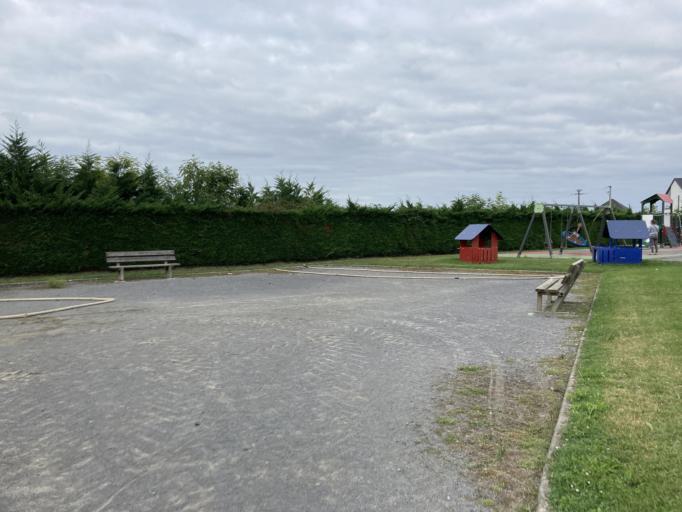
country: FR
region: Aquitaine
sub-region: Departement des Pyrenees-Atlantiques
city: Arbus
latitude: 43.3359
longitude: -0.5058
